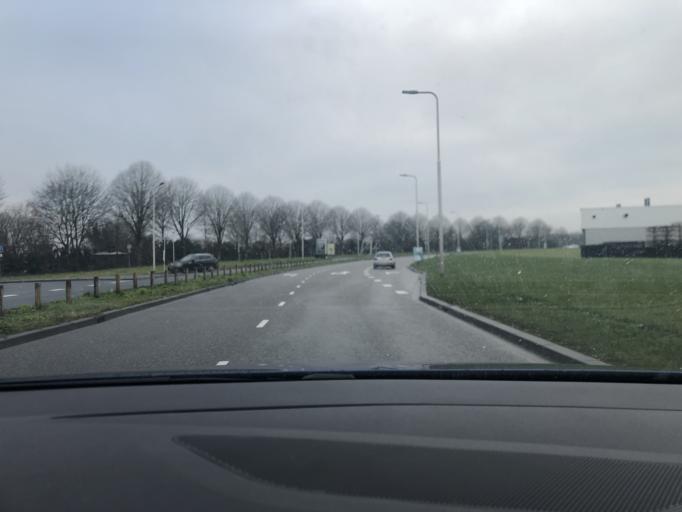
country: NL
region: South Holland
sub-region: Gemeente Hendrik-Ido-Ambacht
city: Hendrik-Ido-Ambacht
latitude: 51.8532
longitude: 4.6479
